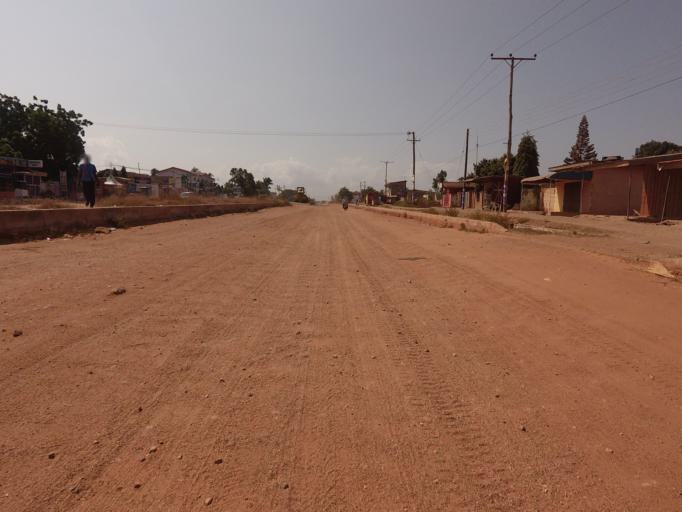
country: GH
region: Greater Accra
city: Teshi Old Town
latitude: 5.6080
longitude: -0.1227
